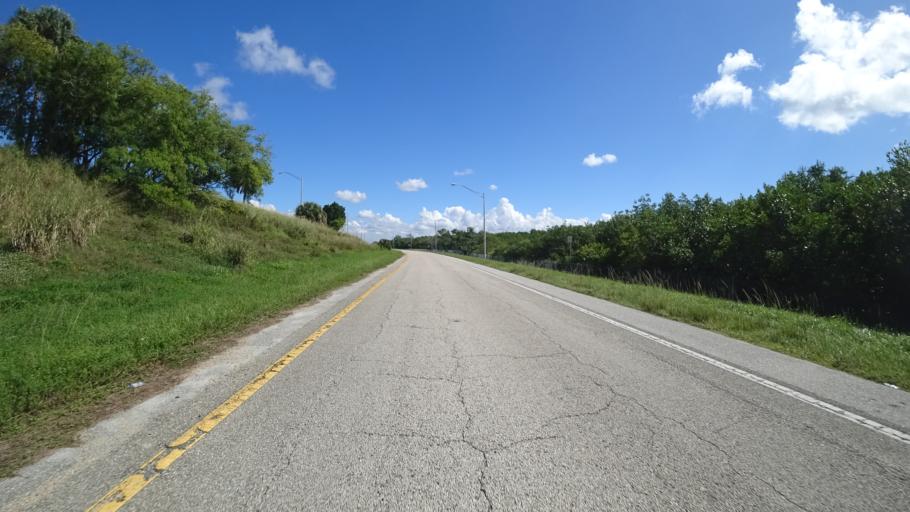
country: US
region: Florida
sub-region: Manatee County
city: Memphis
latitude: 27.5832
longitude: -82.6125
